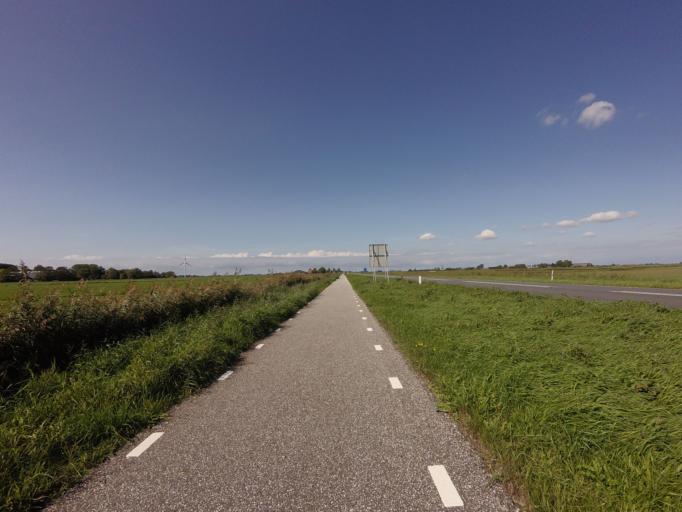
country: NL
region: Friesland
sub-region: Gemeente Littenseradiel
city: Makkum
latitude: 53.1120
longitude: 5.6851
